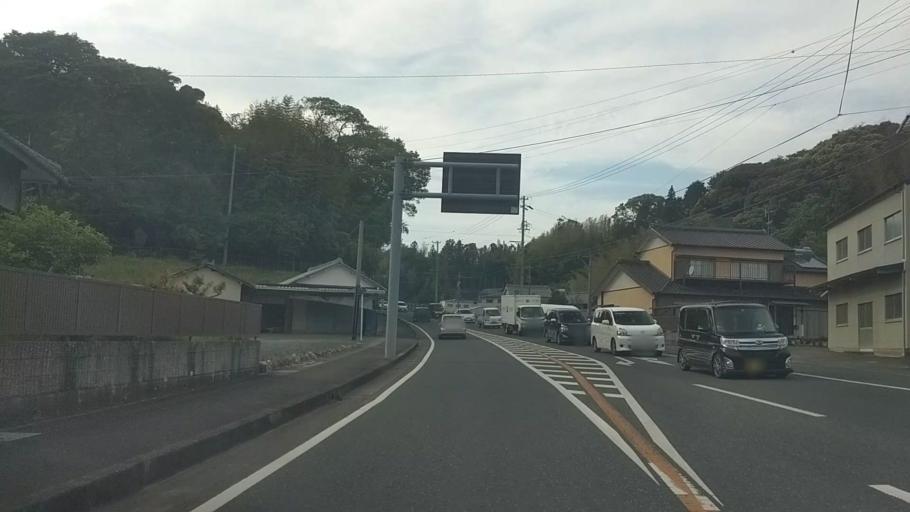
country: JP
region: Shizuoka
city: Hamamatsu
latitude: 34.7625
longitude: 137.6483
